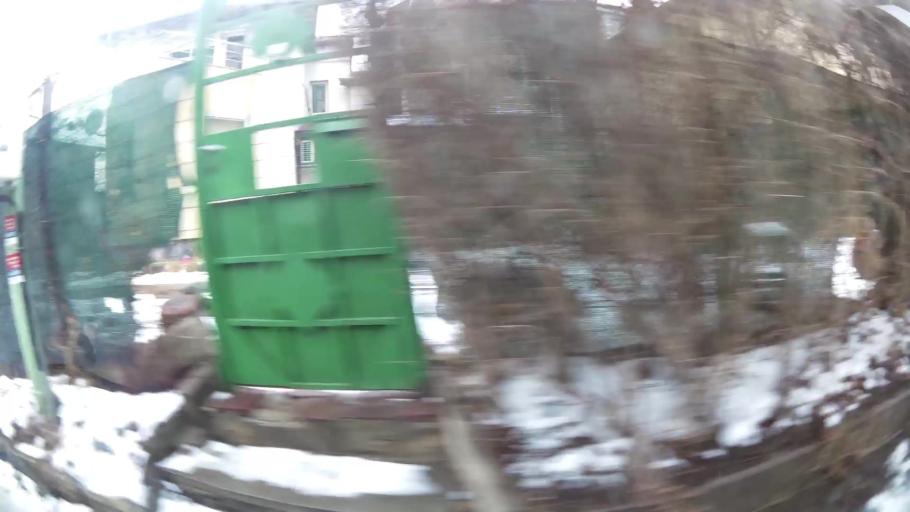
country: BG
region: Sofia-Capital
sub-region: Stolichna Obshtina
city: Sofia
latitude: 42.6791
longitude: 23.2880
